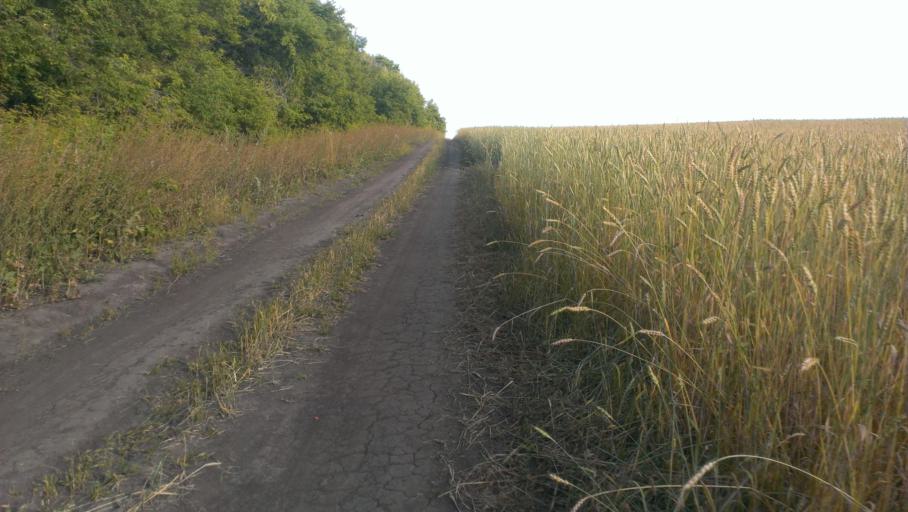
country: RU
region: Altai Krai
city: Gon'ba
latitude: 53.3869
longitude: 83.6006
